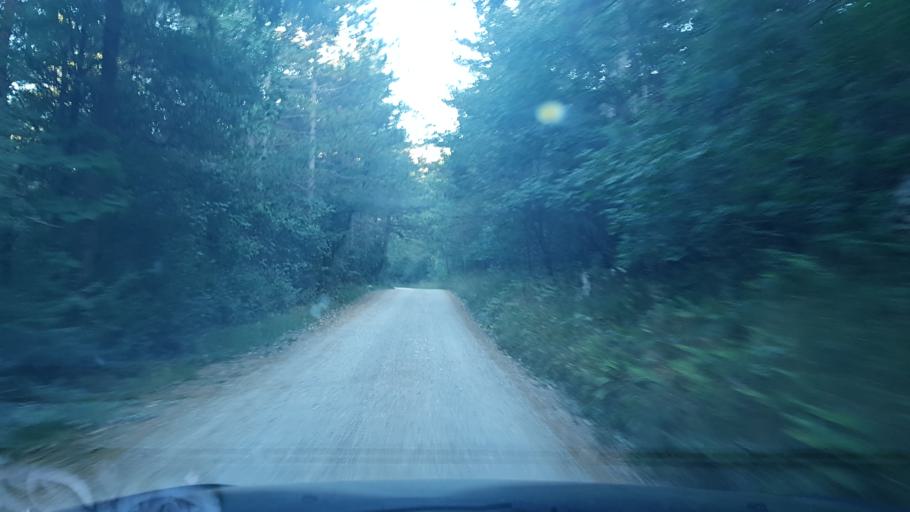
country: SI
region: Vipava
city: Vipava
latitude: 45.7962
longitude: 14.0120
